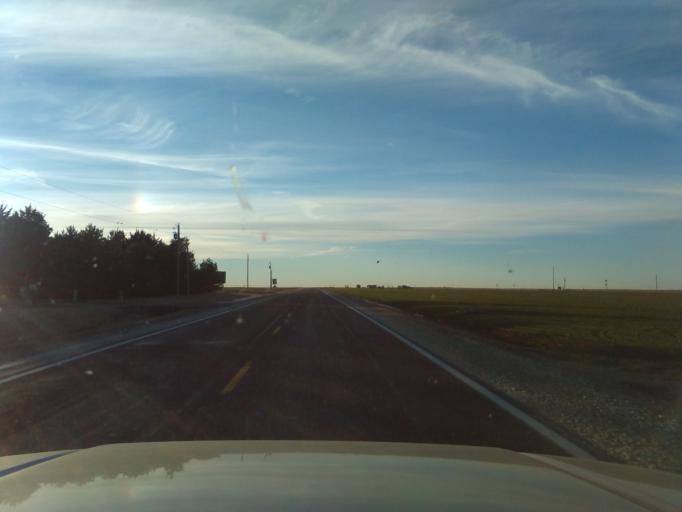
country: US
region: Kansas
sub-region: Logan County
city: Oakley
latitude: 39.1191
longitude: -100.8866
